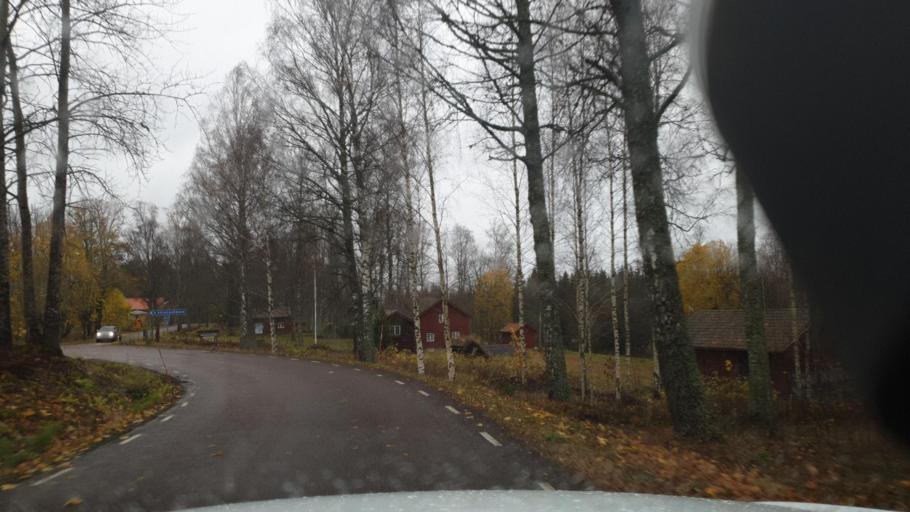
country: SE
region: Vaermland
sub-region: Sunne Kommun
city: Sunne
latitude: 59.7383
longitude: 13.1291
